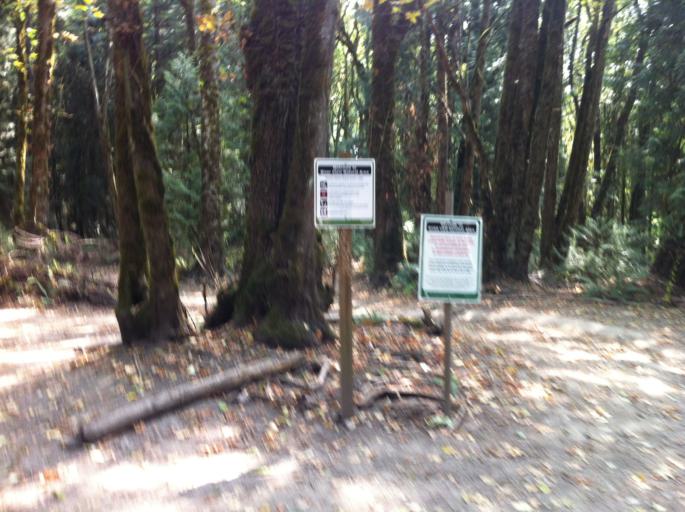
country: US
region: Oregon
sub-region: Clackamas County
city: Lake Oswego
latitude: 45.4554
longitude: -122.6741
